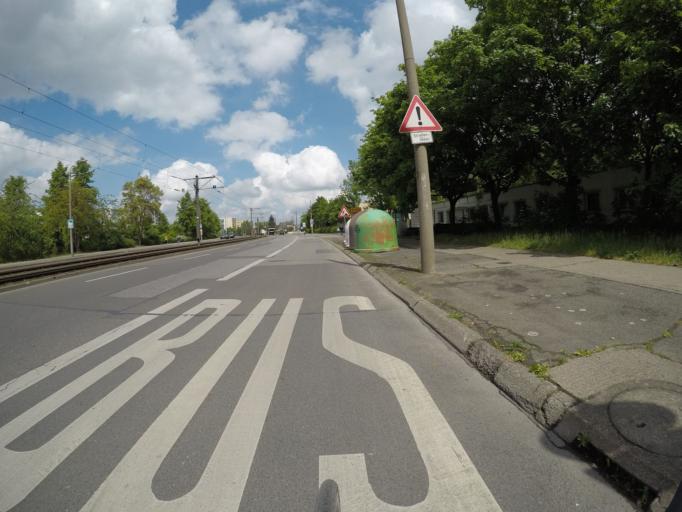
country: DE
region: Berlin
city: Marzahn
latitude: 52.5430
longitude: 13.5646
